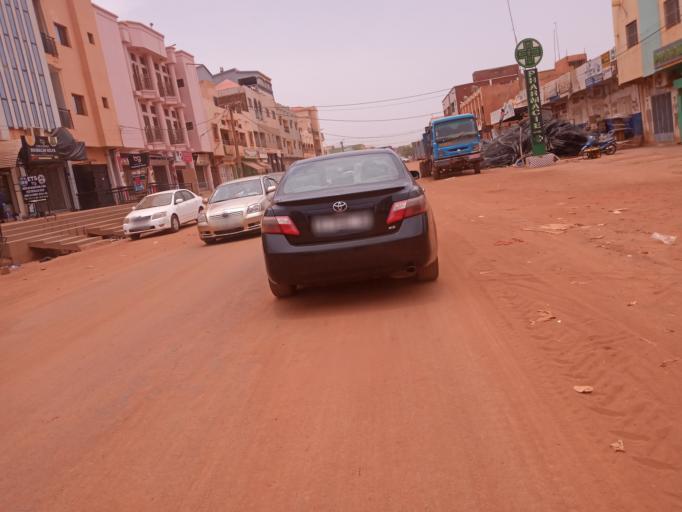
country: ML
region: Bamako
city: Bamako
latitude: 12.5782
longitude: -8.0144
